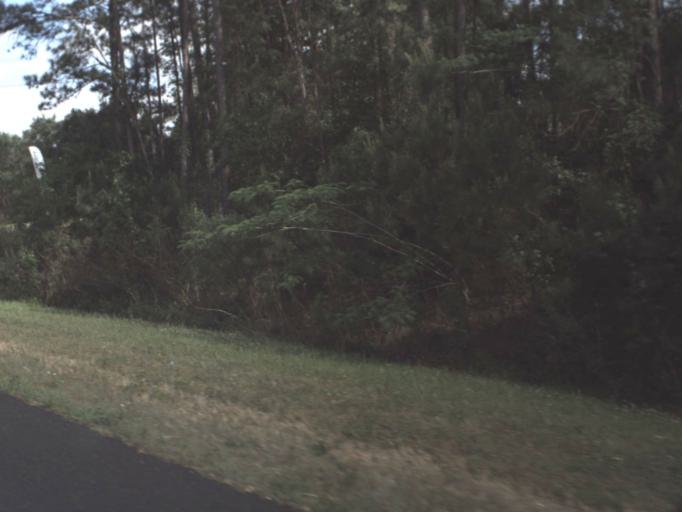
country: US
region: Florida
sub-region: Marion County
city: Ocala
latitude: 29.2310
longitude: -82.2598
